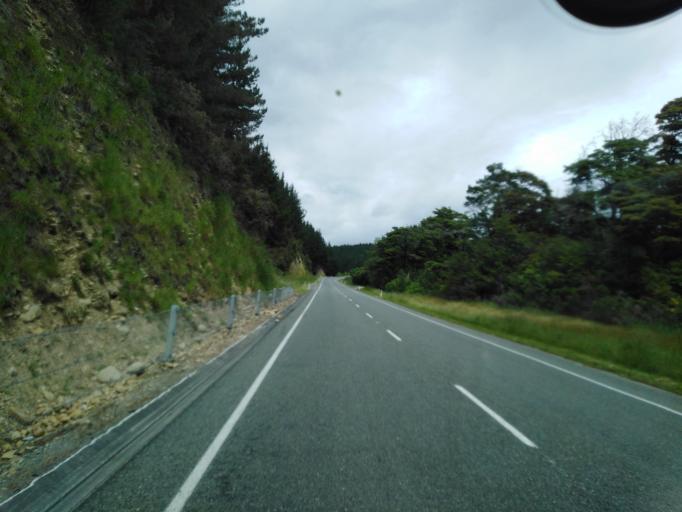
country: NZ
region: Tasman
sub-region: Tasman District
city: Wakefield
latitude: -41.4762
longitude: 172.9327
